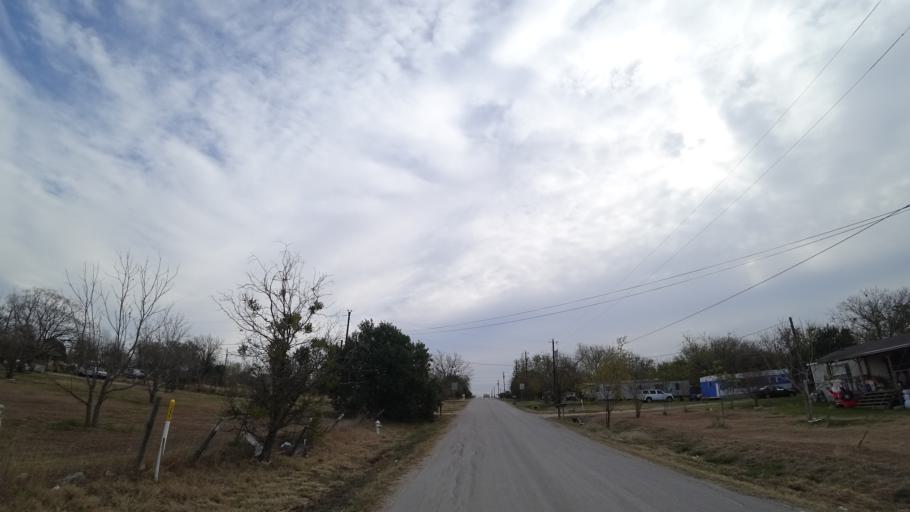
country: US
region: Texas
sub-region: Travis County
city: Onion Creek
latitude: 30.1482
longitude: -97.6692
